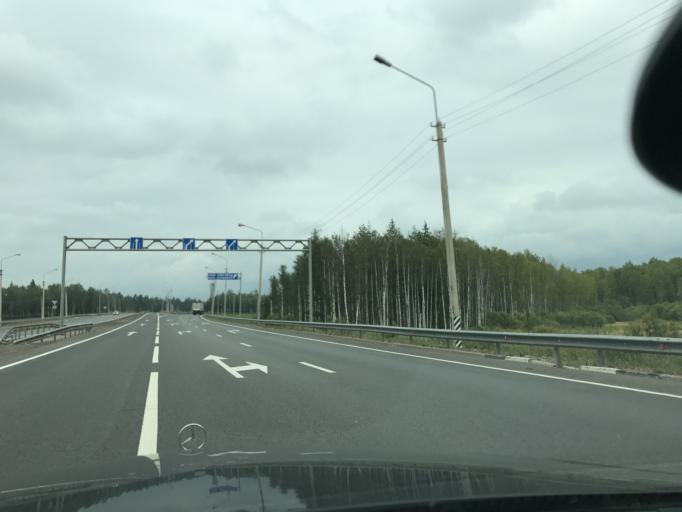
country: RU
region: Vladimir
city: Kameshkovo
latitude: 56.1906
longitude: 40.9509
